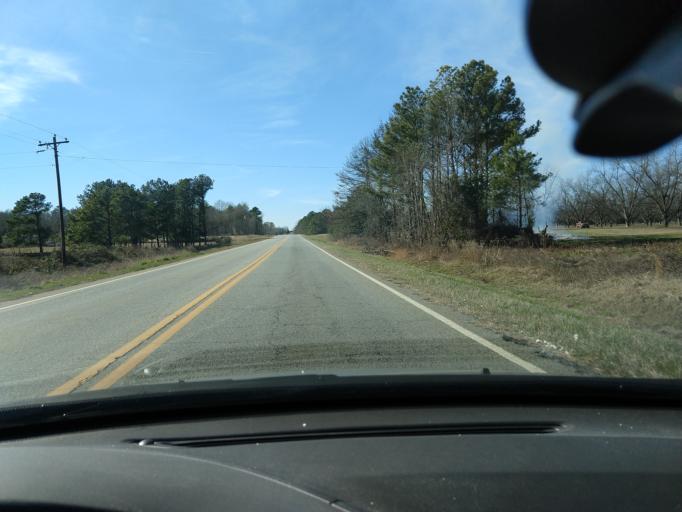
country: US
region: Georgia
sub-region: Dooly County
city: Unadilla
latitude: 32.3399
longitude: -83.8014
